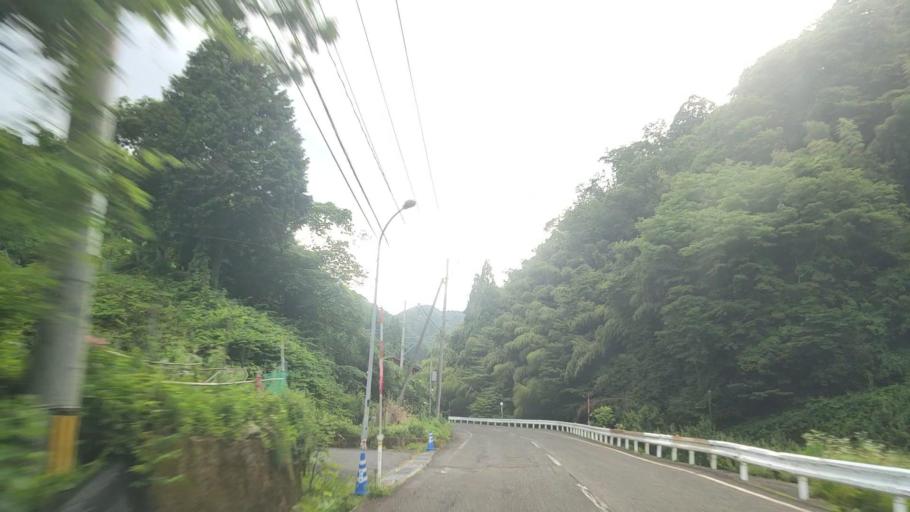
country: JP
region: Tottori
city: Kurayoshi
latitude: 35.3227
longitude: 134.0225
